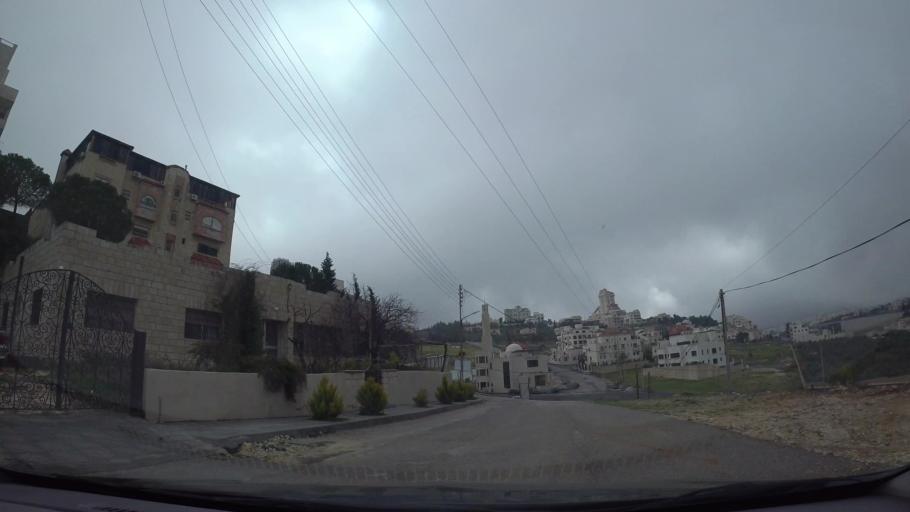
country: JO
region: Amman
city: Umm as Summaq
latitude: 31.9187
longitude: 35.8656
